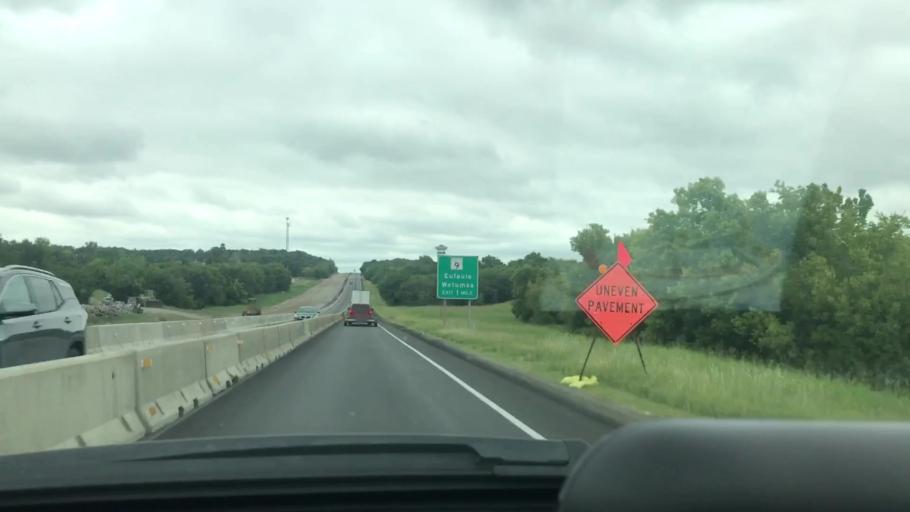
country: US
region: Oklahoma
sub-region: McIntosh County
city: Eufaula
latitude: 35.2776
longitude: -95.5931
